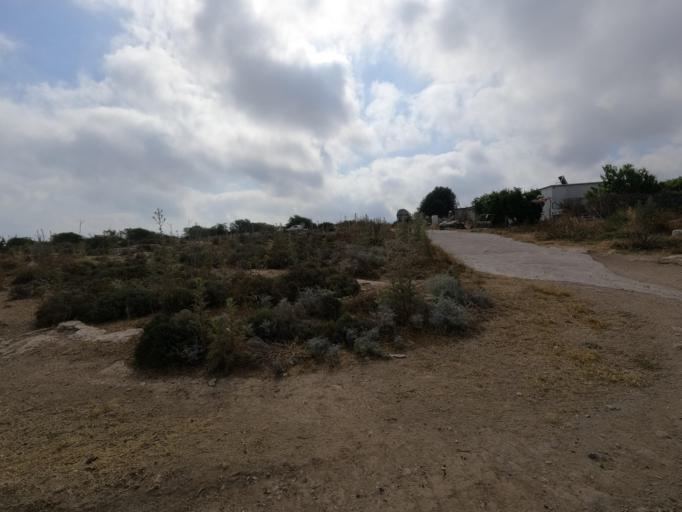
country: CY
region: Ammochostos
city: Ayia Napa
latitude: 35.0149
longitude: 34.0070
